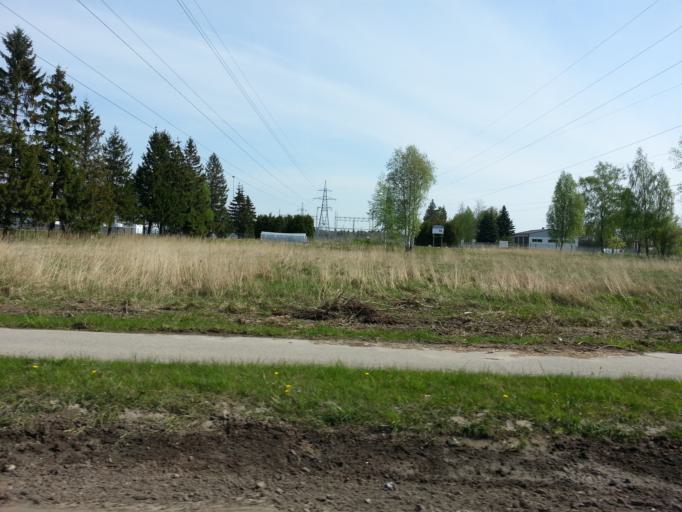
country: LT
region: Panevezys
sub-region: Panevezys City
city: Panevezys
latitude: 55.7606
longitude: 24.3045
